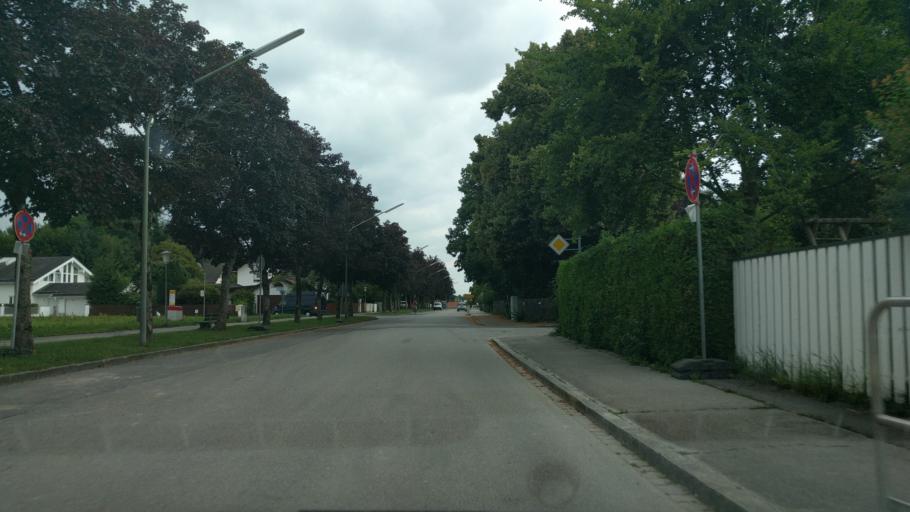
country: DE
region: Bavaria
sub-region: Upper Bavaria
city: Grunwald
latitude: 48.0409
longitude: 11.5293
